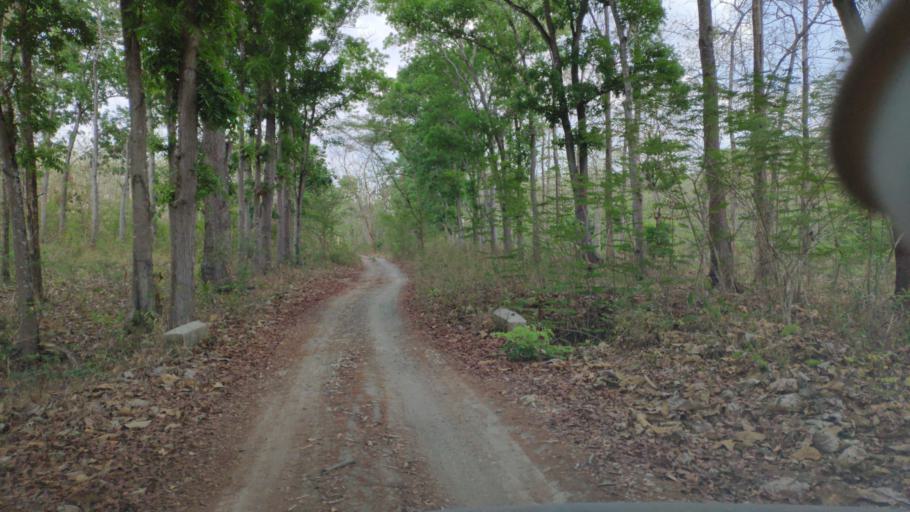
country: ID
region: Central Java
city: Singonegoro
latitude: -6.9917
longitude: 111.5350
